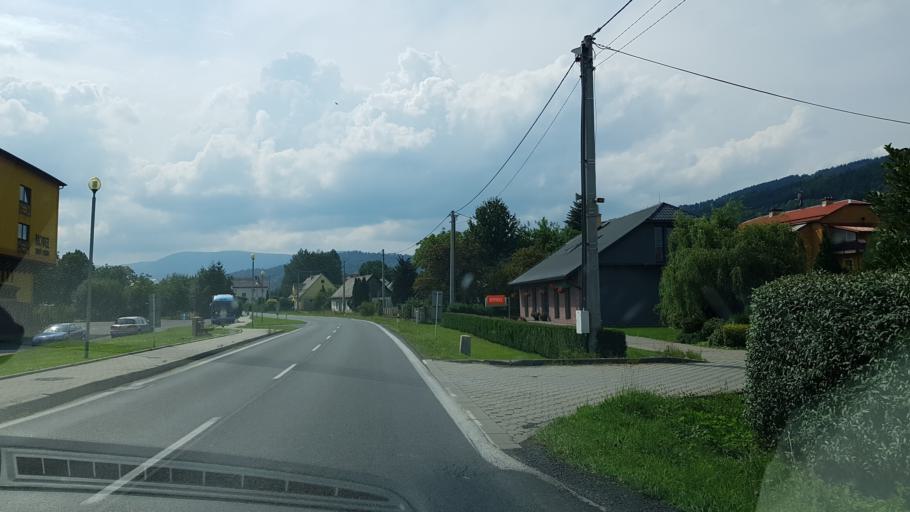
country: CZ
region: Olomoucky
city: Ceska Ves
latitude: 50.2569
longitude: 17.2264
